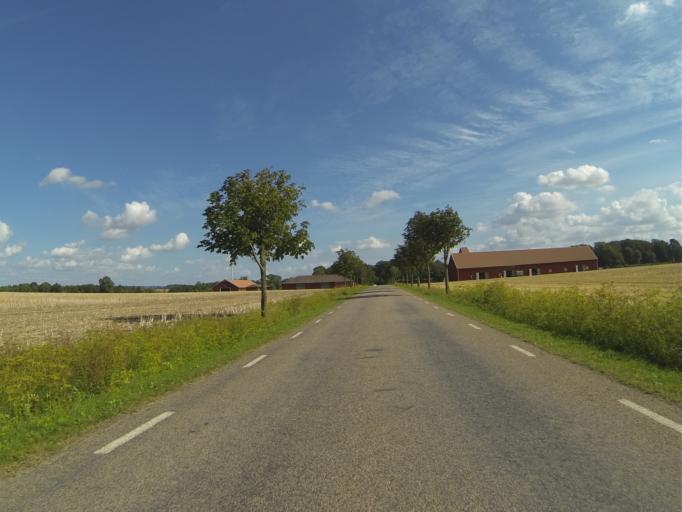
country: SE
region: Skane
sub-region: Lunds Kommun
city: Lund
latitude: 55.7684
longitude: 13.2486
